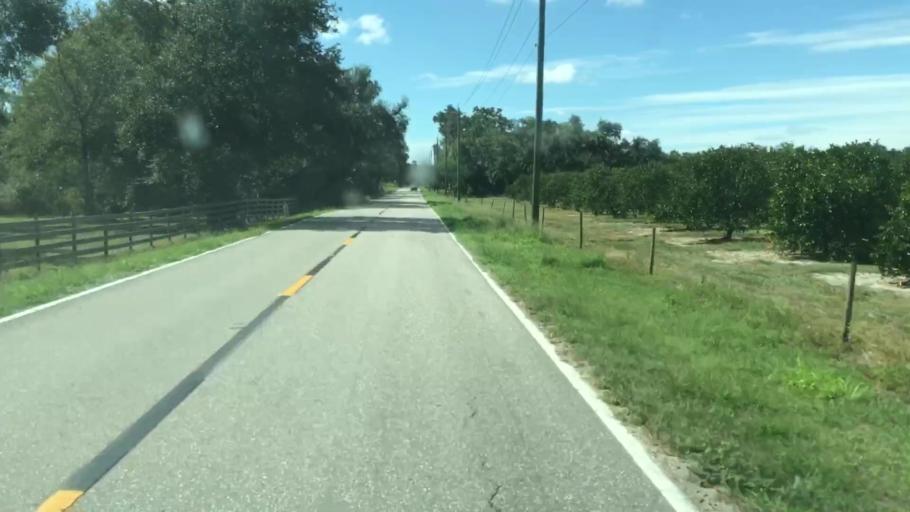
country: US
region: Florida
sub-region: Lee County
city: Alva
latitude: 26.7260
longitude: -81.6282
